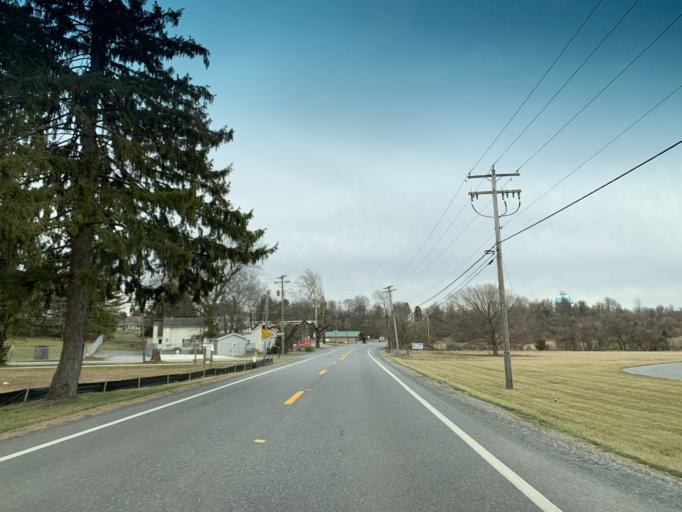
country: US
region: West Virginia
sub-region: Jefferson County
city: Charles Town
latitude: 39.2784
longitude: -77.8532
